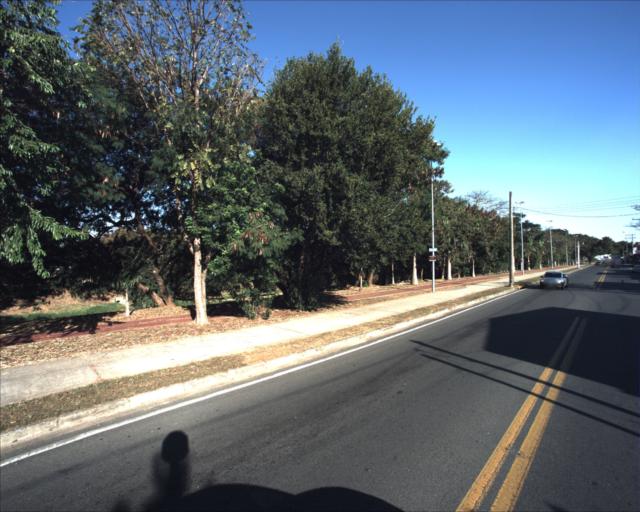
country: BR
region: Sao Paulo
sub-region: Sorocaba
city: Sorocaba
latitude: -23.4712
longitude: -47.4422
